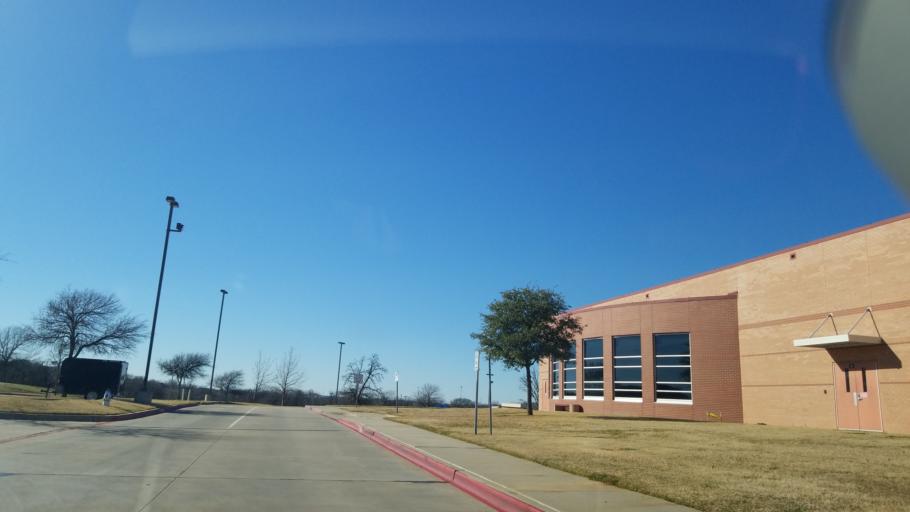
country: US
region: Texas
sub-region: Denton County
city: Corinth
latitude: 33.1468
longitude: -97.0818
